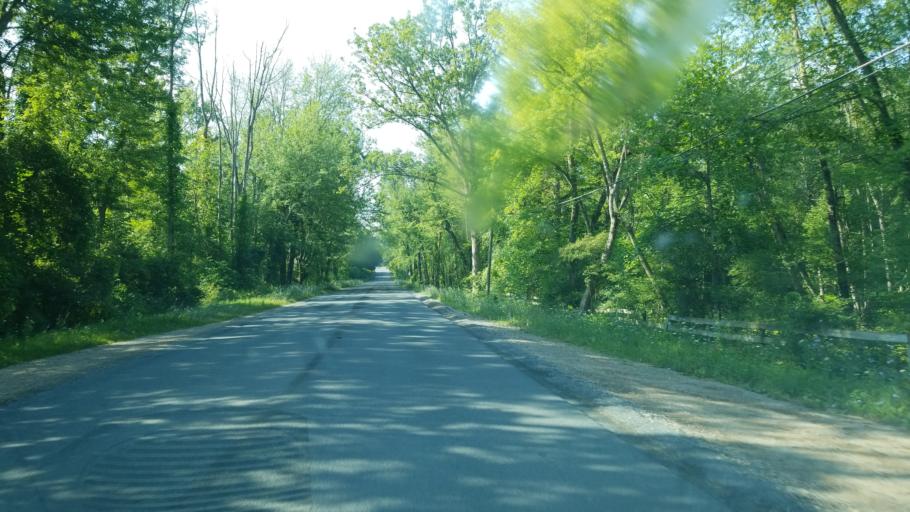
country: US
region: Michigan
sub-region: Kent County
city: Sparta
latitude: 43.1224
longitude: -85.6508
